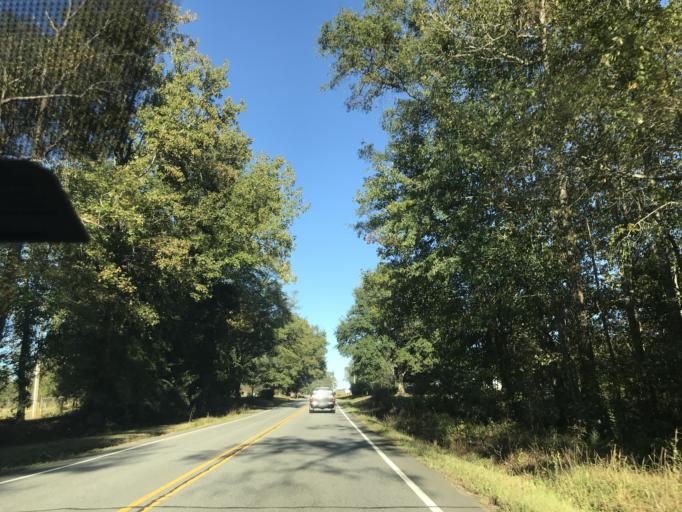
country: US
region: South Carolina
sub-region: Spartanburg County
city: Mayo
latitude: 35.1111
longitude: -81.8271
